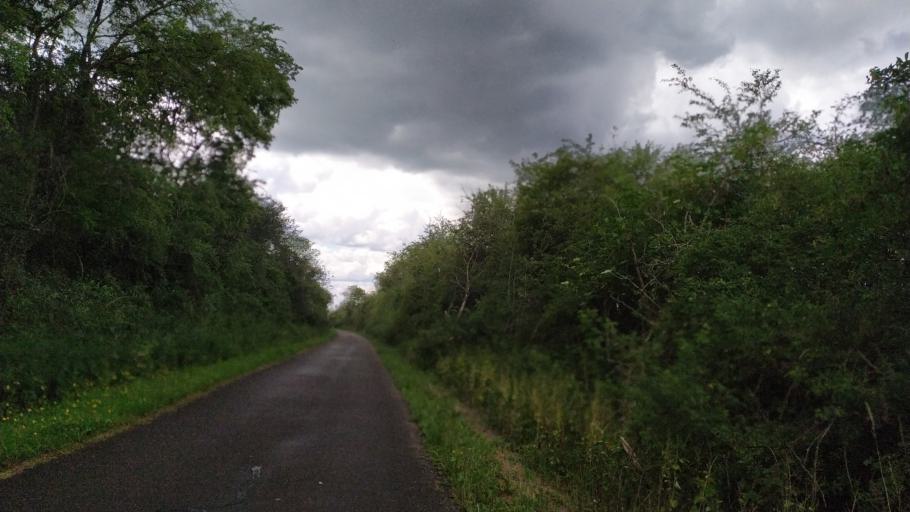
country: BE
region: Wallonia
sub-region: Province de Namur
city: Rochefort
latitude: 50.1595
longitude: 5.1981
